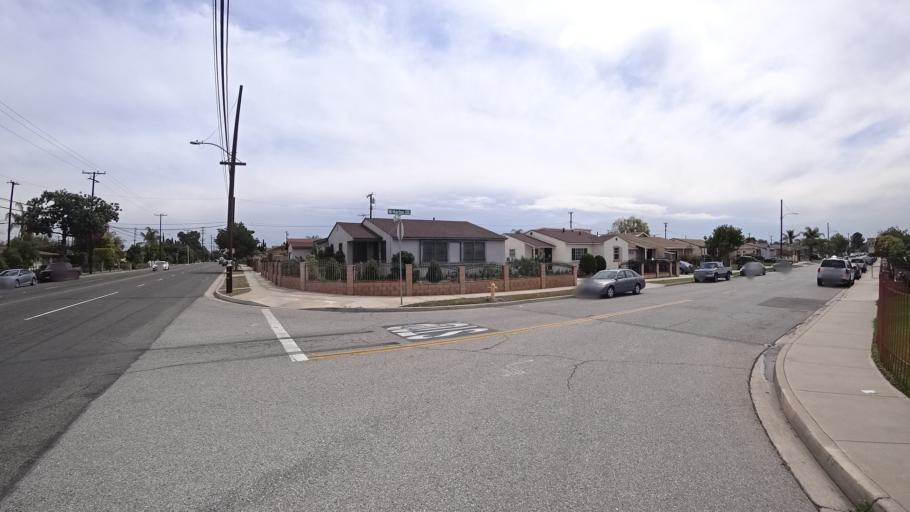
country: US
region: California
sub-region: Los Angeles County
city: Baldwin Park
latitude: 34.0920
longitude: -117.9808
